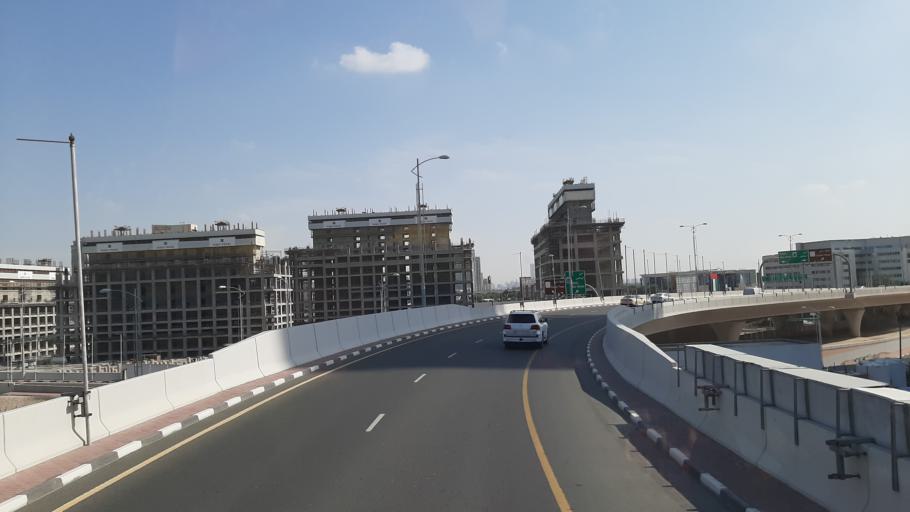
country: AE
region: Dubai
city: Dubai
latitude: 25.1001
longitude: 55.1570
